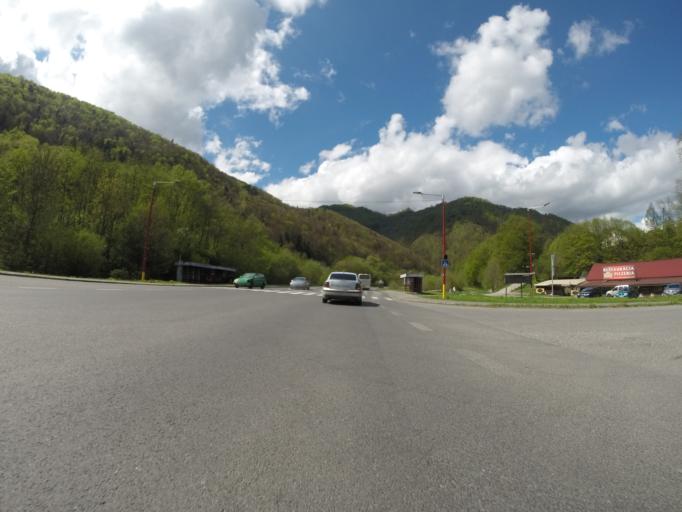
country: SK
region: Banskobystricky
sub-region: Okres Banska Bystrica
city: Brezno
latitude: 48.8039
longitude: 19.5572
